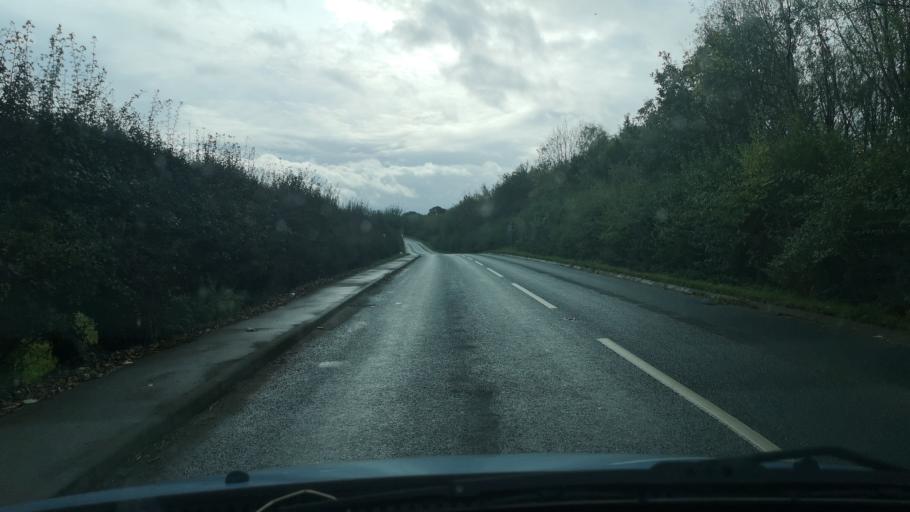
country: GB
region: England
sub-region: City and Borough of Wakefield
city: Fitzwilliam
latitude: 53.6468
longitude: -1.3866
